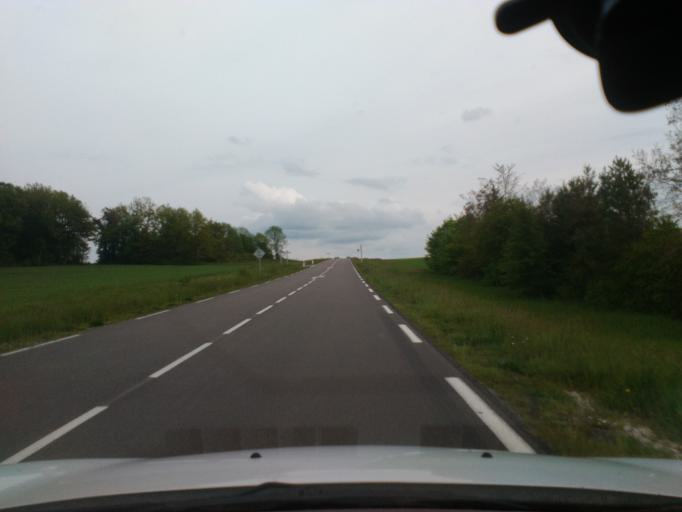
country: FR
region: Champagne-Ardenne
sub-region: Departement de la Haute-Marne
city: Lavilleneuve-au-Roi
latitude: 48.2034
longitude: 4.9376
